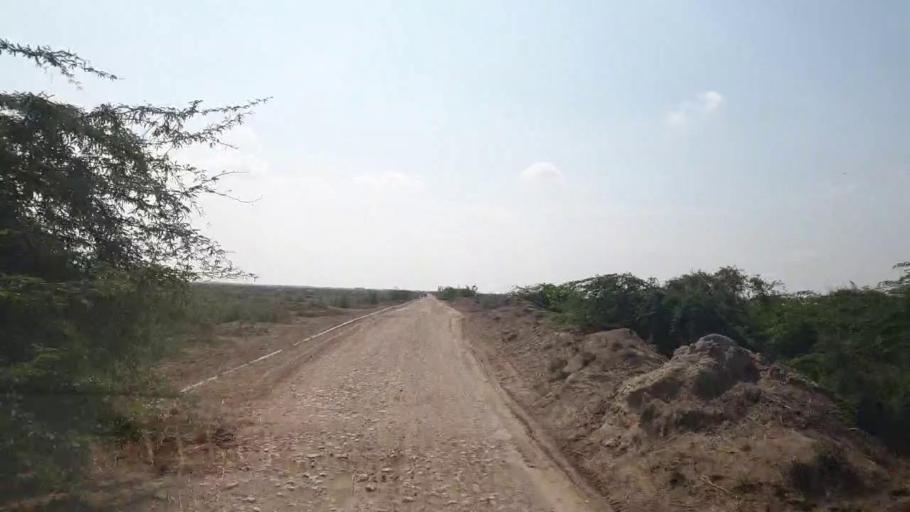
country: PK
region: Sindh
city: Badin
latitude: 24.5115
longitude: 68.6081
